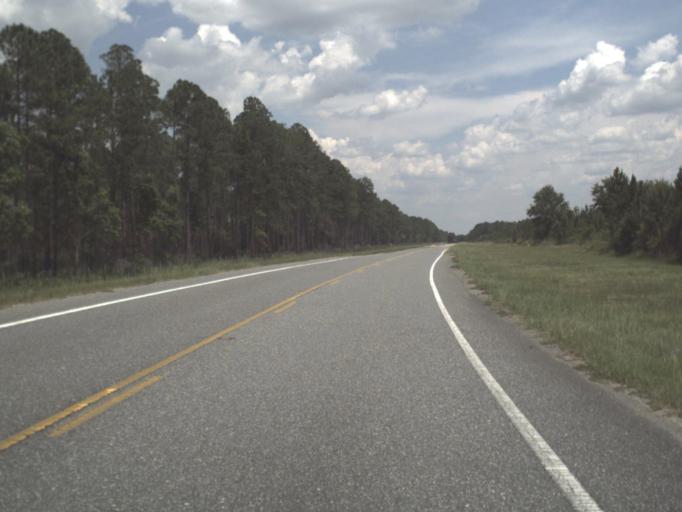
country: US
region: Florida
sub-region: Bradford County
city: Starke
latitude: 29.9965
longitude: -82.0290
